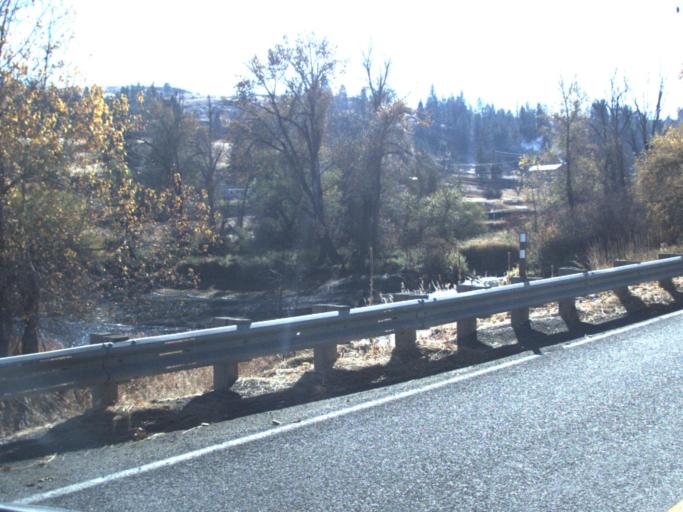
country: CA
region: British Columbia
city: Grand Forks
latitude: 48.8818
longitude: -118.6037
